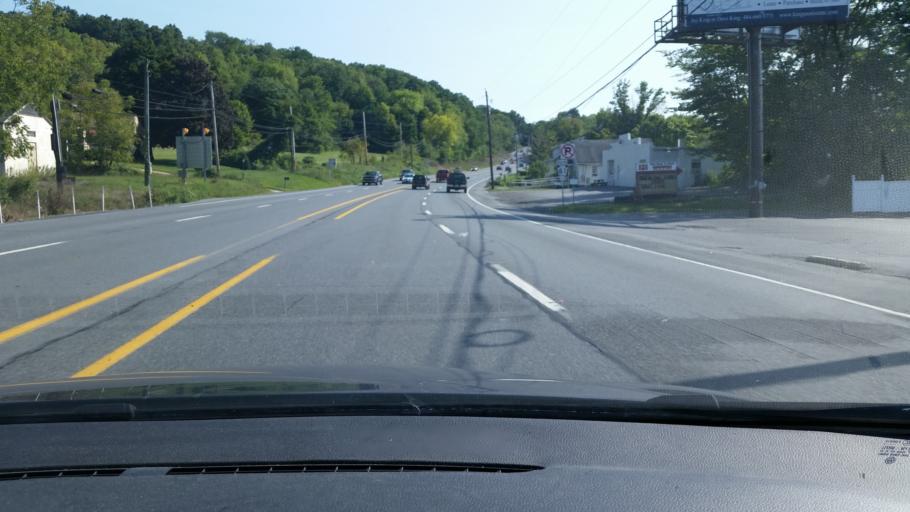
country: US
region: Pennsylvania
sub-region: Berks County
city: Hamburg
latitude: 40.5346
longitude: -75.9753
